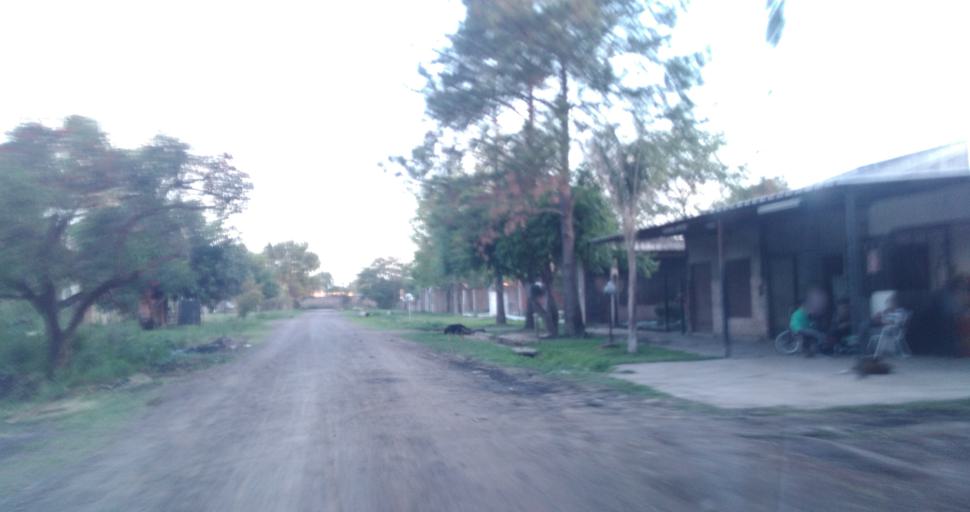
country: AR
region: Chaco
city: Fontana
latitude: -27.4024
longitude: -59.0020
